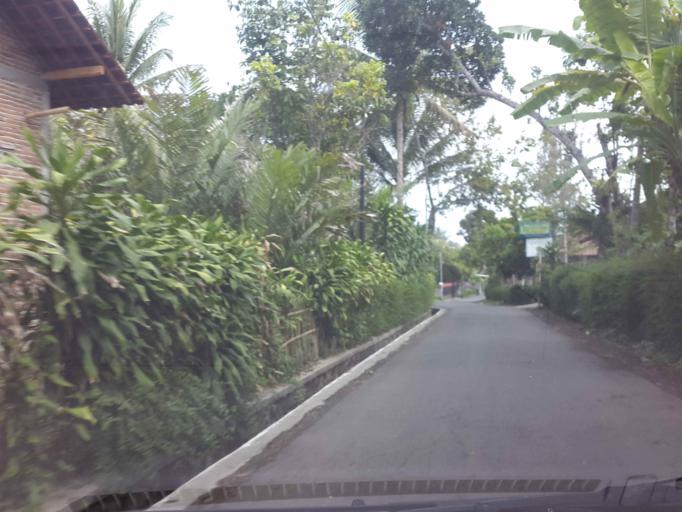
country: ID
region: Central Java
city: Salatiga
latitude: -7.3398
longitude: 110.5169
